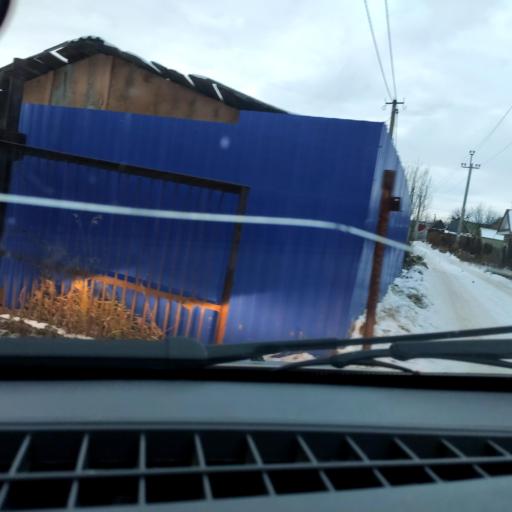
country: RU
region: Bashkortostan
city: Avdon
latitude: 54.6799
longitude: 55.7880
